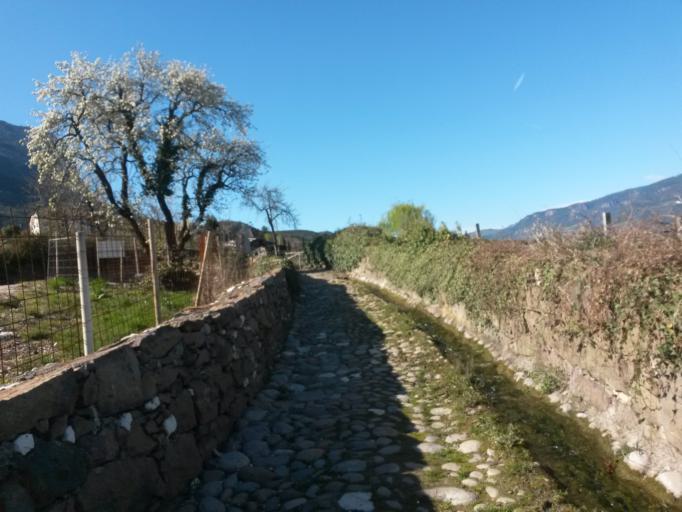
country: IT
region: Trentino-Alto Adige
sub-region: Bolzano
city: San Paolo
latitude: 46.4648
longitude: 11.2532
